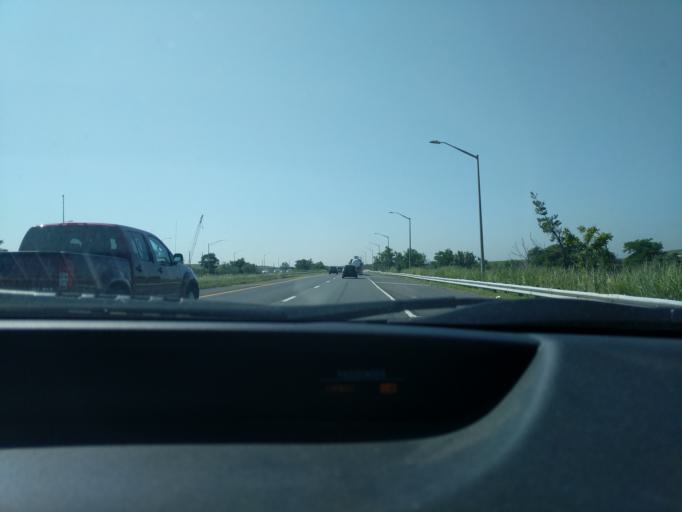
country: US
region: New York
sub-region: Richmond County
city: Bloomfield
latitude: 40.5794
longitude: -74.1912
